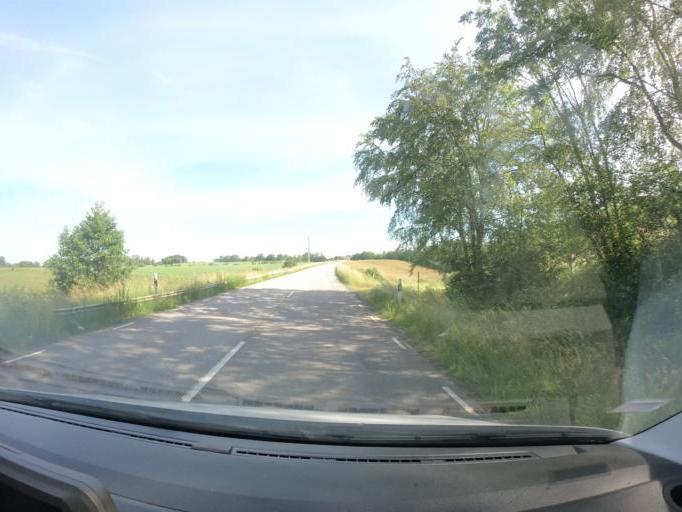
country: SE
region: Skane
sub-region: Bastads Kommun
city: Forslov
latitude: 56.3858
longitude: 12.8033
